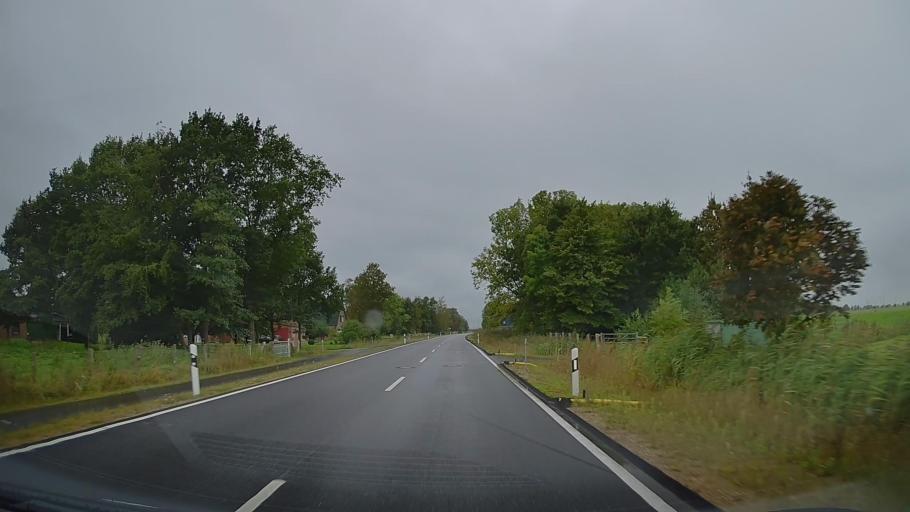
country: DE
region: Schleswig-Holstein
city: Brokdorf
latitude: 53.8678
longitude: 9.3105
